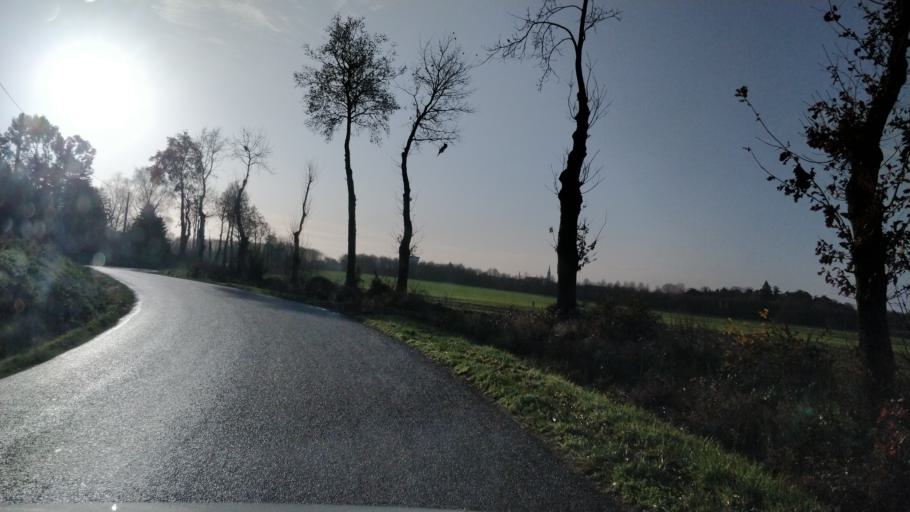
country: FR
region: Brittany
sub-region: Departement d'Ille-et-Vilaine
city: Chavagne
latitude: 48.0637
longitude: -1.7905
